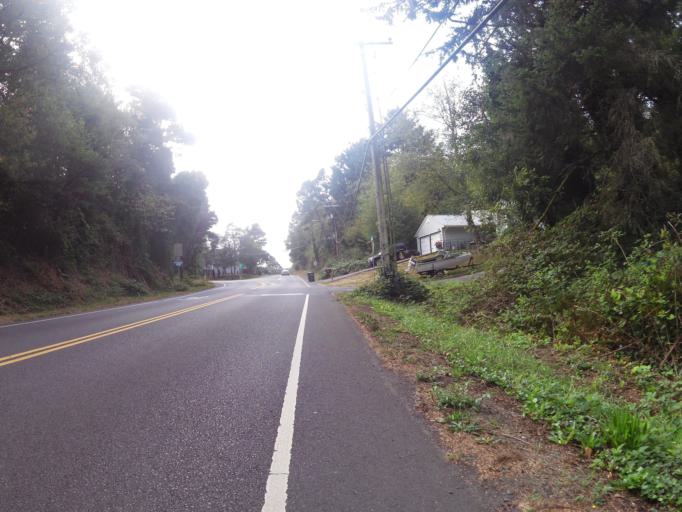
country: US
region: Oregon
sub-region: Lincoln County
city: Newport
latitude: 44.6548
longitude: -124.0564
